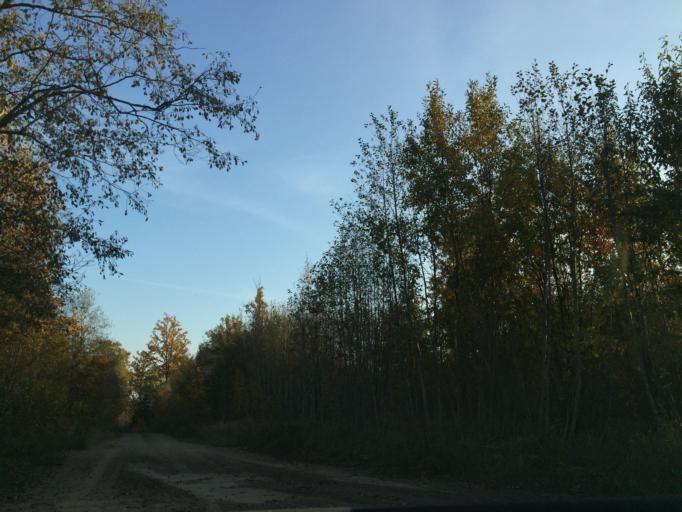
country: LV
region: Vainode
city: Vainode
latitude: 56.5858
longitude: 21.8344
